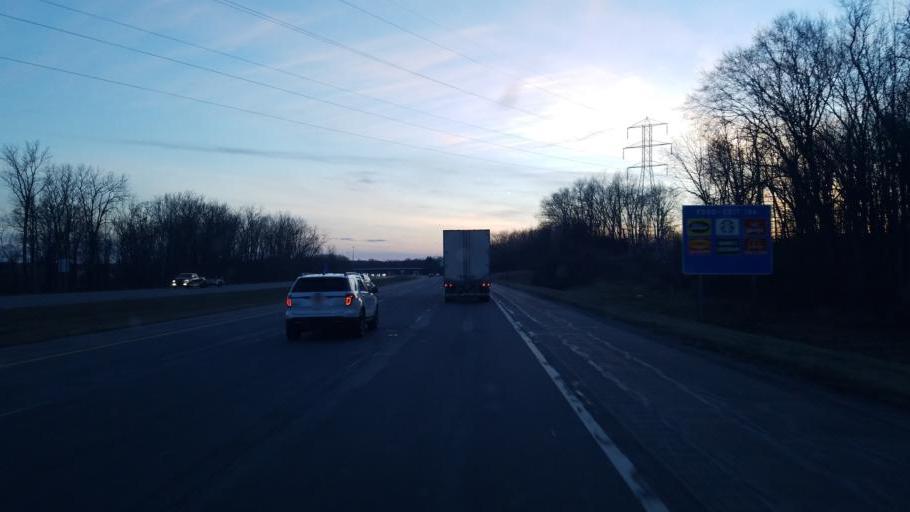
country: US
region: Ohio
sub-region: Ashland County
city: Ashland
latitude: 40.8668
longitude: -82.2428
